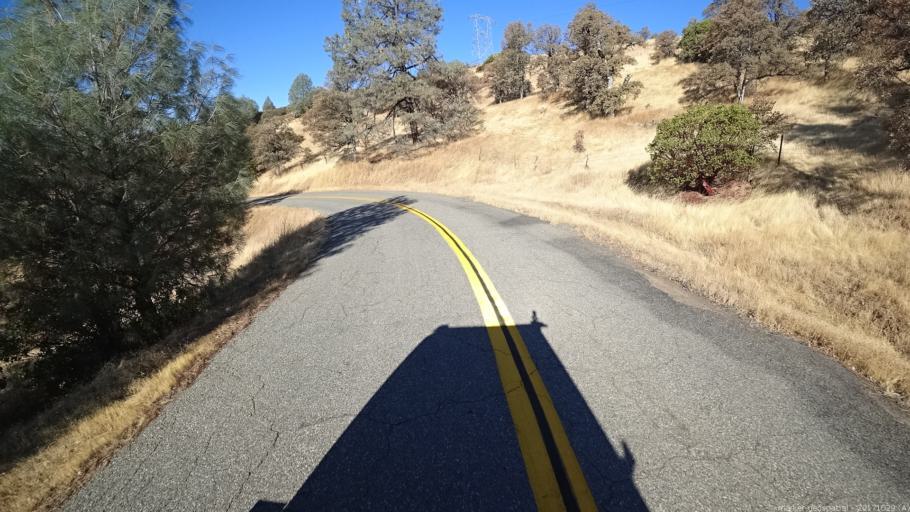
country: US
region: California
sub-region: Trinity County
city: Lewiston
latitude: 40.3643
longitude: -122.8816
